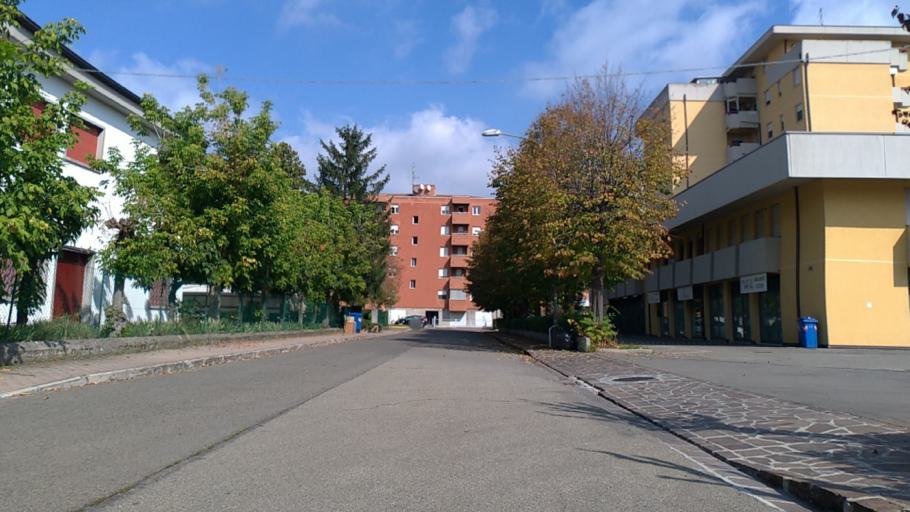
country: IT
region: Emilia-Romagna
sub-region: Provincia di Modena
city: Carpi Centro
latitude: 44.7710
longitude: 10.8728
